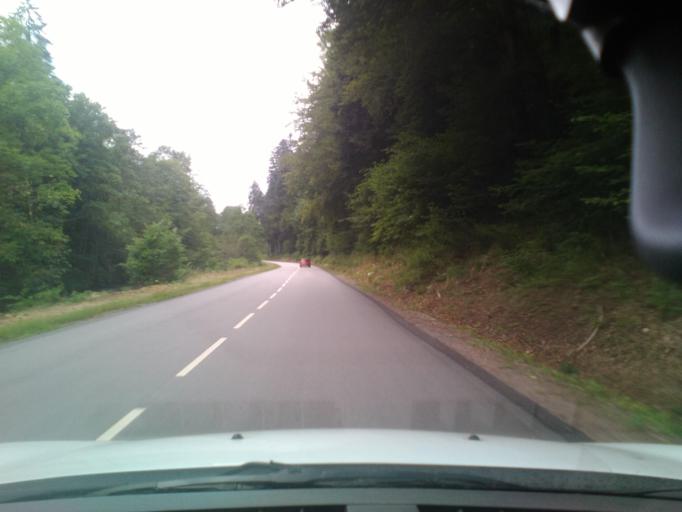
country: FR
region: Lorraine
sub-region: Departement des Vosges
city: Gerardmer
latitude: 48.1099
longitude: 6.8580
